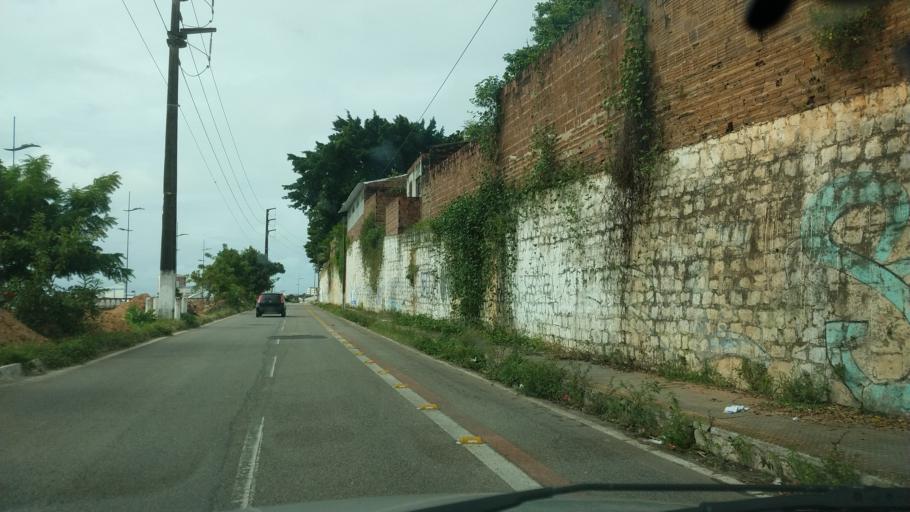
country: BR
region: Rio Grande do Norte
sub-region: Natal
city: Natal
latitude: -5.7839
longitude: -35.2104
